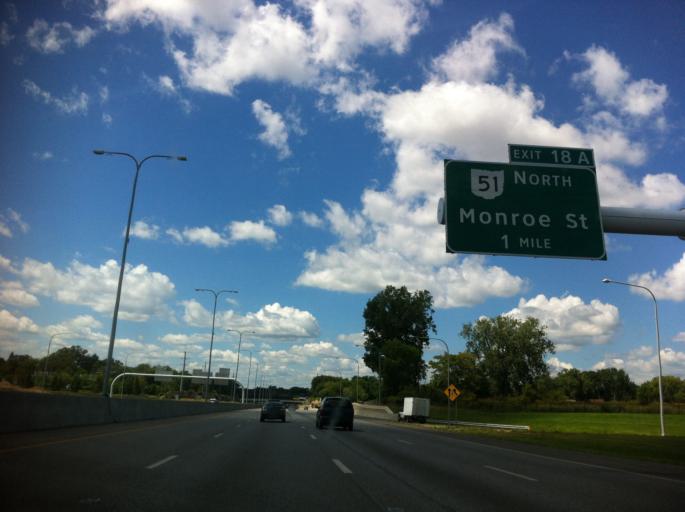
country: US
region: Ohio
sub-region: Lucas County
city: Toledo
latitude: 41.6803
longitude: -83.5923
